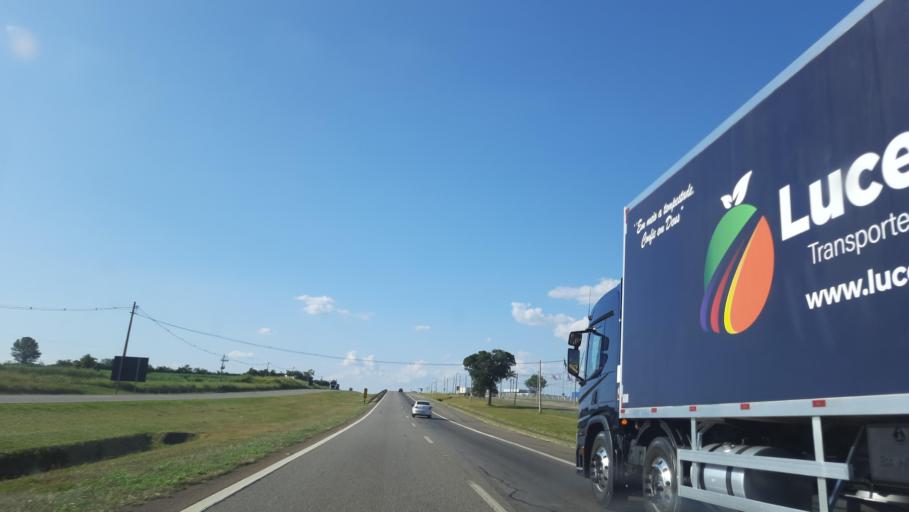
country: BR
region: Sao Paulo
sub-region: Santo Antonio De Posse
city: Santo Antonio de Posse
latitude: -22.6073
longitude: -47.0074
